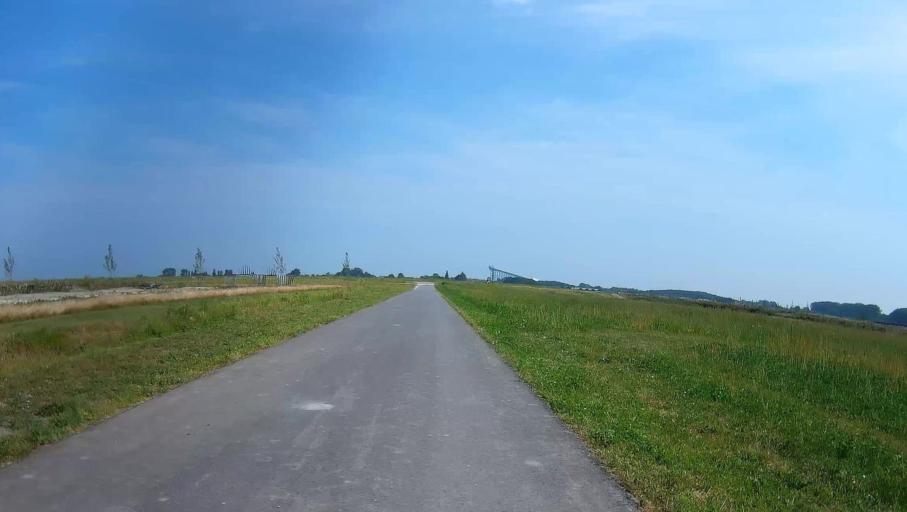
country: NL
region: South Holland
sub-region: Gemeente Pijnacker-Nootdorp
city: Pijnacker
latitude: 52.0606
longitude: 4.4337
